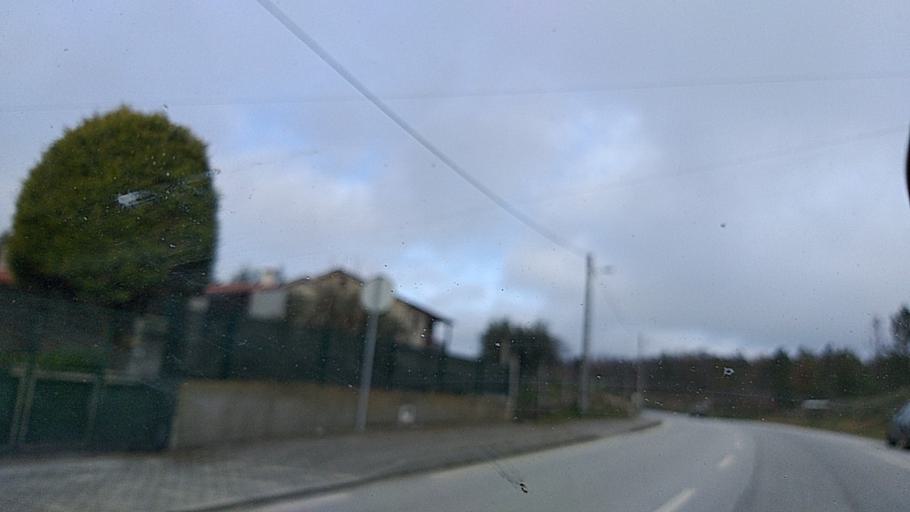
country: PT
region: Guarda
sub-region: Aguiar da Beira
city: Aguiar da Beira
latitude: 40.7247
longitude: -7.4936
